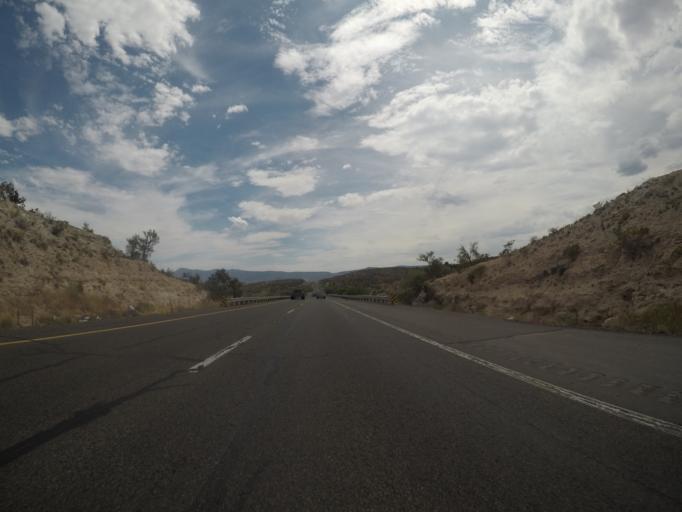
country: US
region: Arizona
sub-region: Yavapai County
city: Lake Montezuma
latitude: 34.6294
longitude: -111.8364
